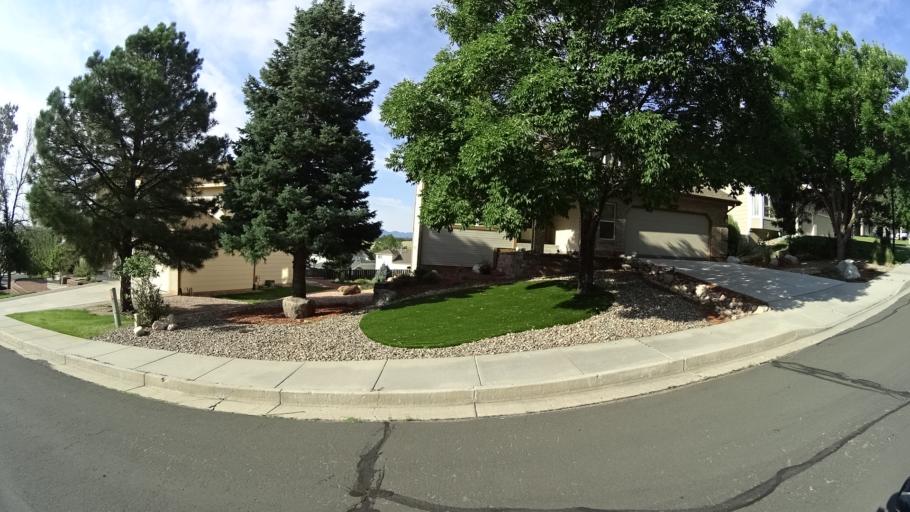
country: US
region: Colorado
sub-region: El Paso County
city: Air Force Academy
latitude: 38.9260
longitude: -104.8518
